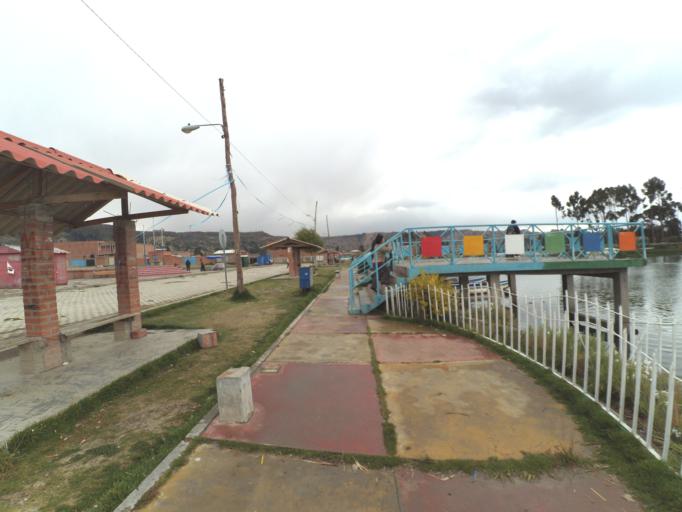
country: BO
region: La Paz
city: La Paz
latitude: -16.5781
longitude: -68.1676
